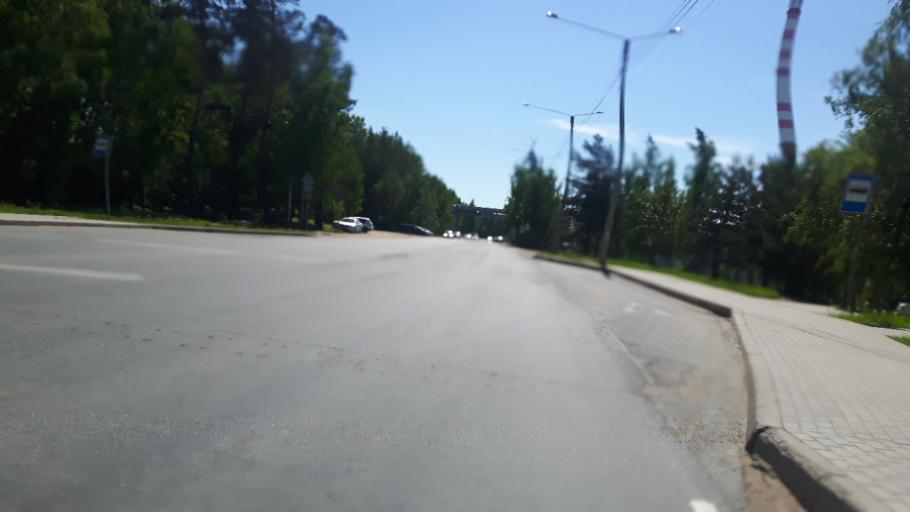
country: RU
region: Leningrad
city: Sosnovyy Bor
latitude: 59.8551
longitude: 29.0553
